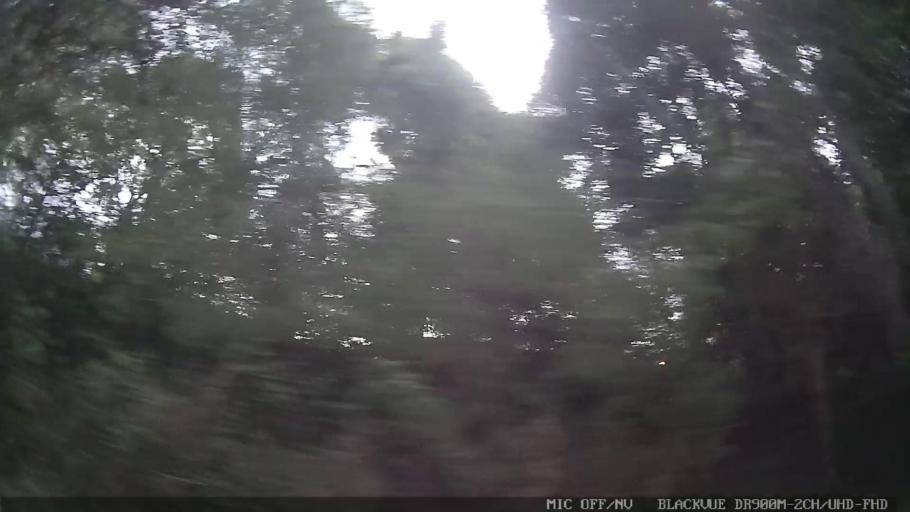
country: BR
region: Sao Paulo
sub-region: Amparo
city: Amparo
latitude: -22.7228
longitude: -46.7697
